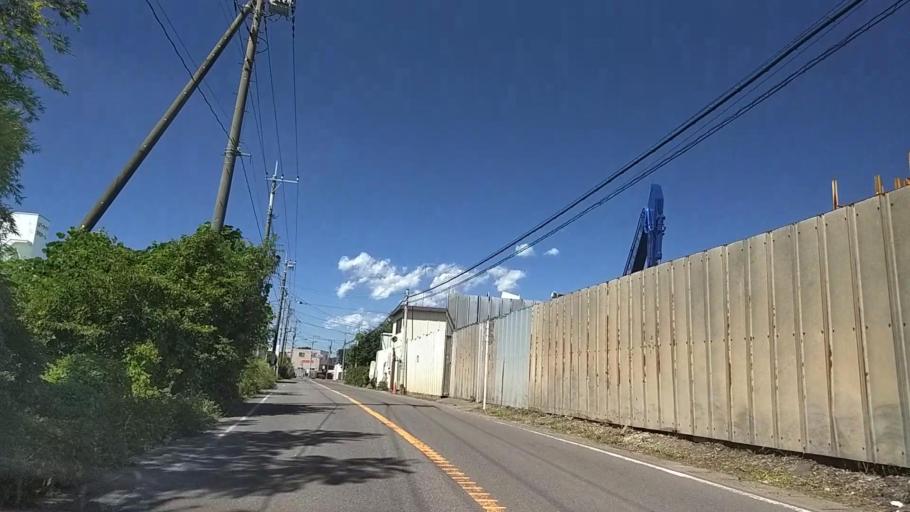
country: JP
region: Kanagawa
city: Zama
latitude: 35.5363
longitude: 139.3478
